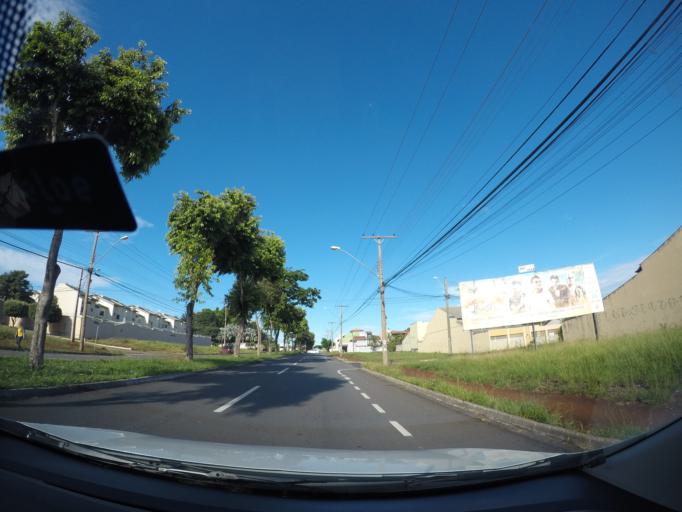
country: BR
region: Goias
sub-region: Goiania
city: Goiania
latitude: -16.7341
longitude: -49.3039
